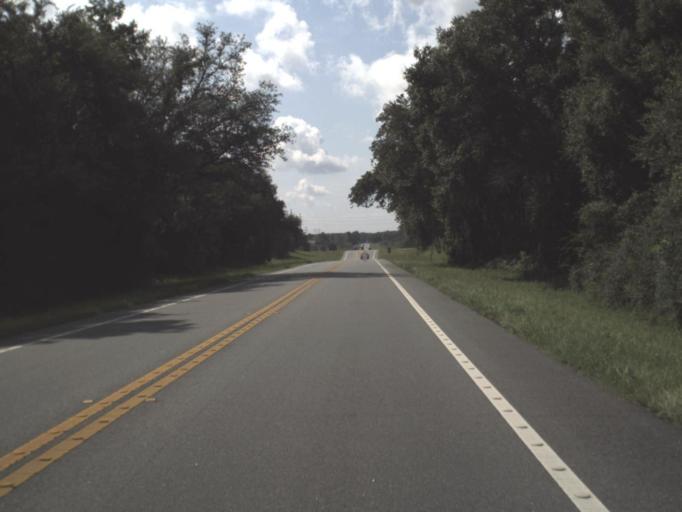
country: US
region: Florida
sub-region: Citrus County
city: Citrus Springs
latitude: 28.9824
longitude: -82.4316
